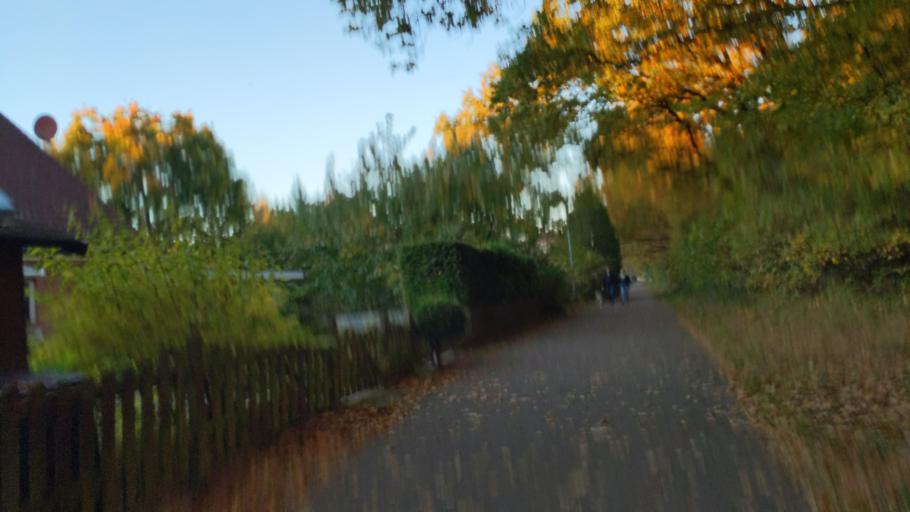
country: DE
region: Schleswig-Holstein
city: Gross Gronau
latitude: 53.8578
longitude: 10.7465
